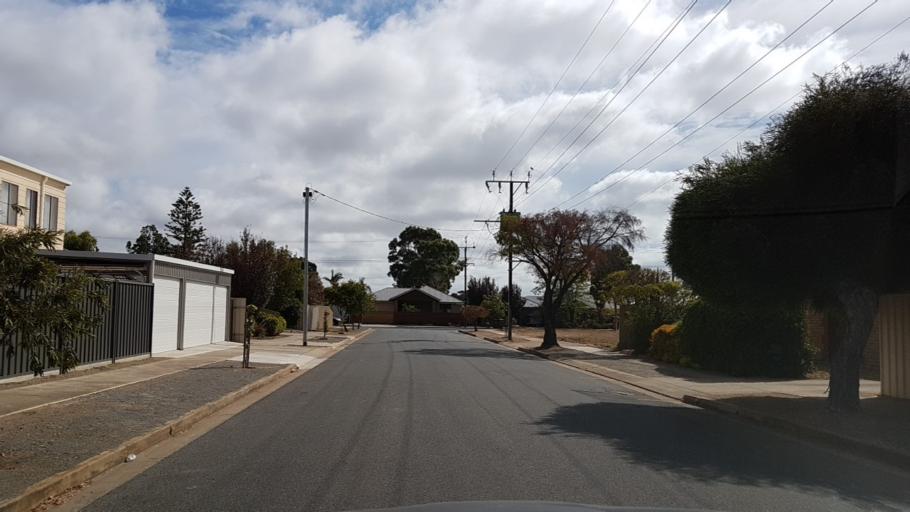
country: AU
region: South Australia
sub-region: Marion
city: Plympton Park
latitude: -34.9834
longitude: 138.5530
